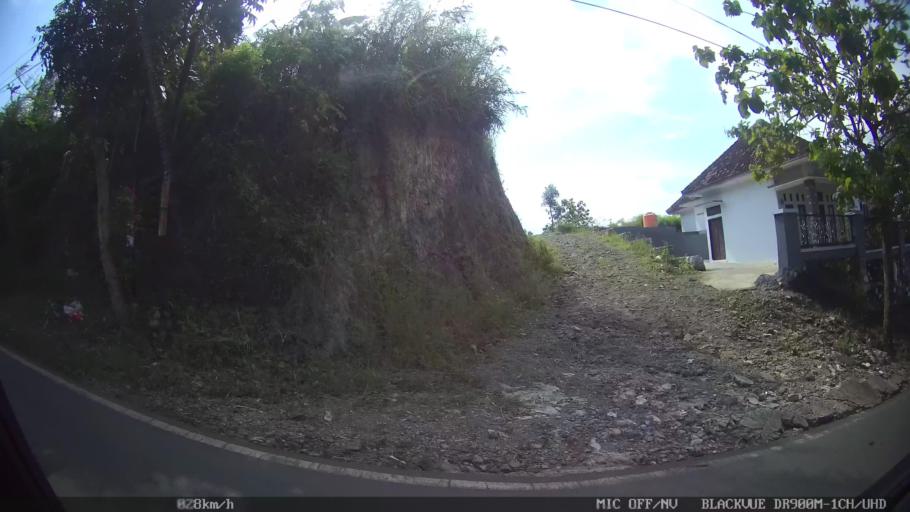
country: ID
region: Lampung
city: Bandarlampung
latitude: -5.4052
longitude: 105.2300
